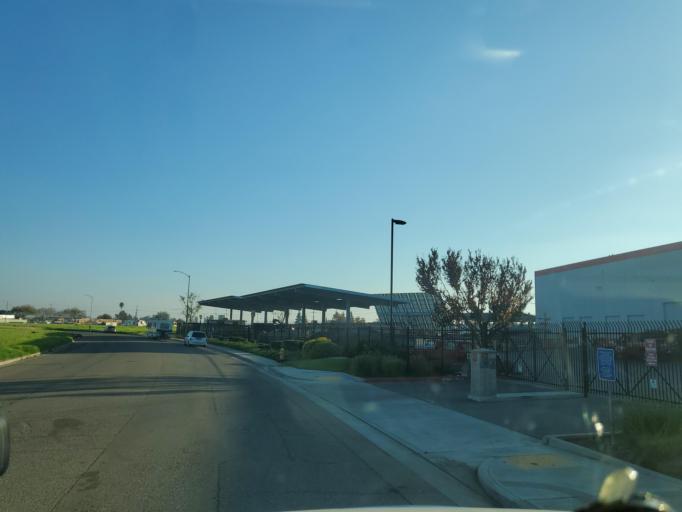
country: US
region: California
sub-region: San Joaquin County
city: Kennedy
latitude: 37.9088
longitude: -121.2226
